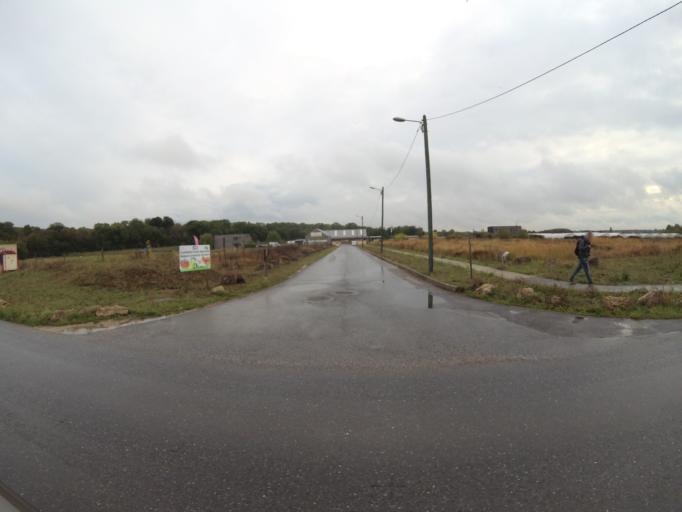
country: FR
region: Ile-de-France
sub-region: Departement de Seine-et-Marne
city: Chanteloup-en-Brie
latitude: 48.8542
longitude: 2.7485
